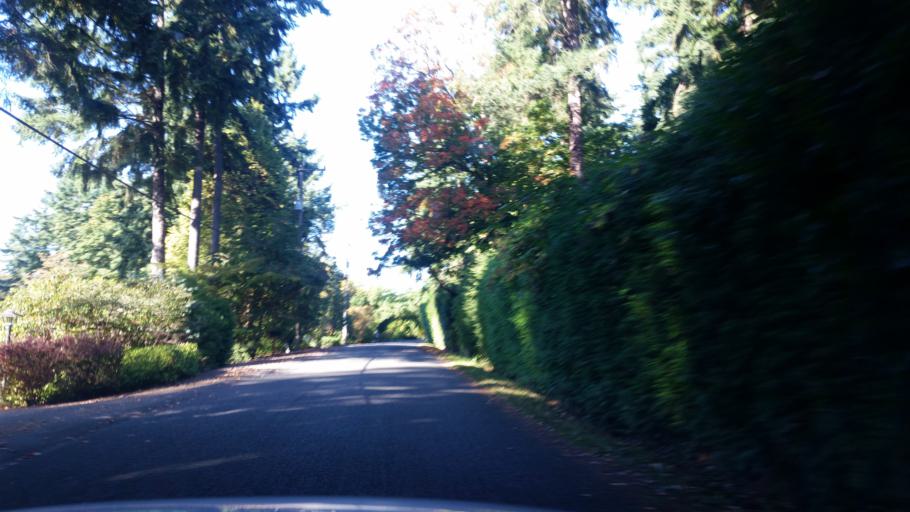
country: US
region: Washington
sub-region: King County
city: Shoreline
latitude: 47.7275
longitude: -122.3664
